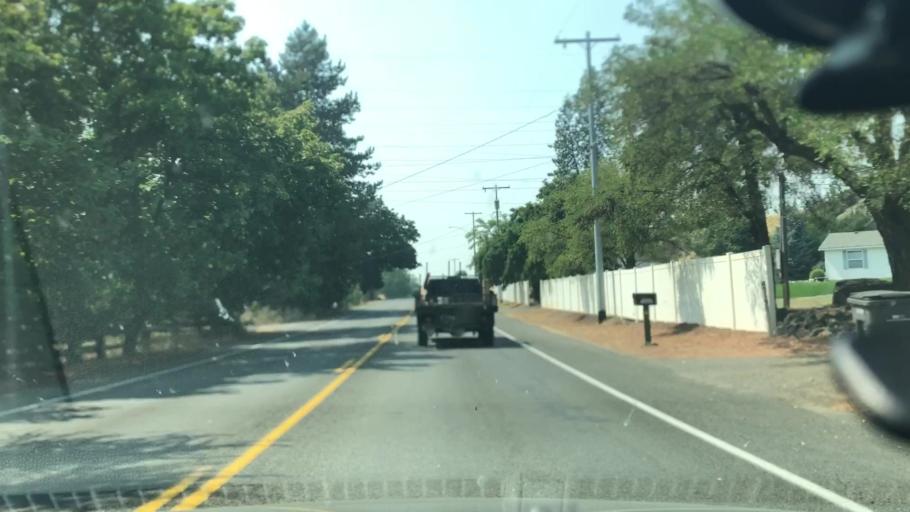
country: US
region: Washington
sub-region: Spokane County
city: Millwood
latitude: 47.6856
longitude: -117.3395
